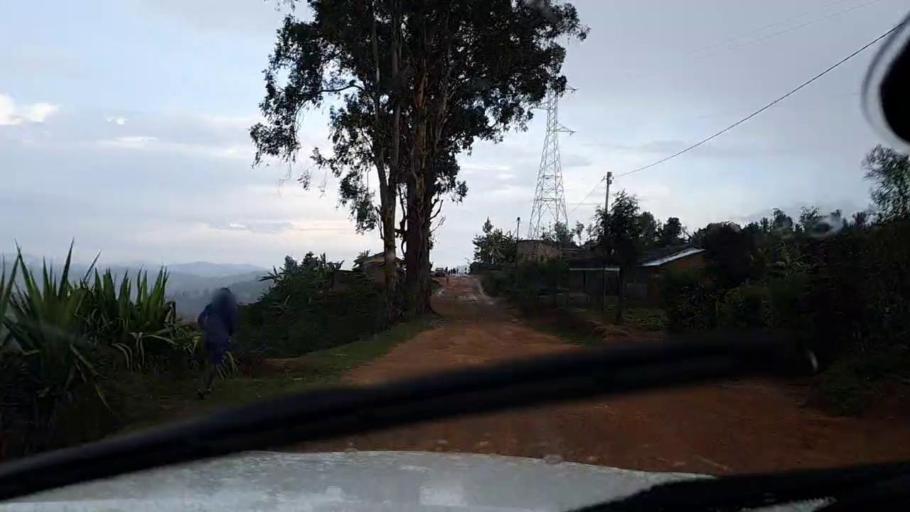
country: BI
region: Kayanza
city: Kayanza
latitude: -2.7762
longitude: 29.5389
